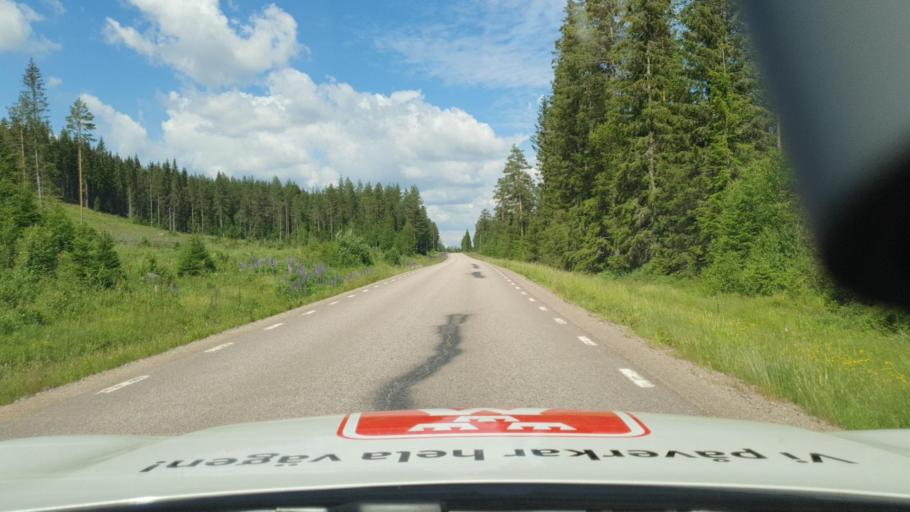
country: SE
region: Vaermland
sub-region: Torsby Kommun
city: Torsby
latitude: 60.4168
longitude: 12.9064
